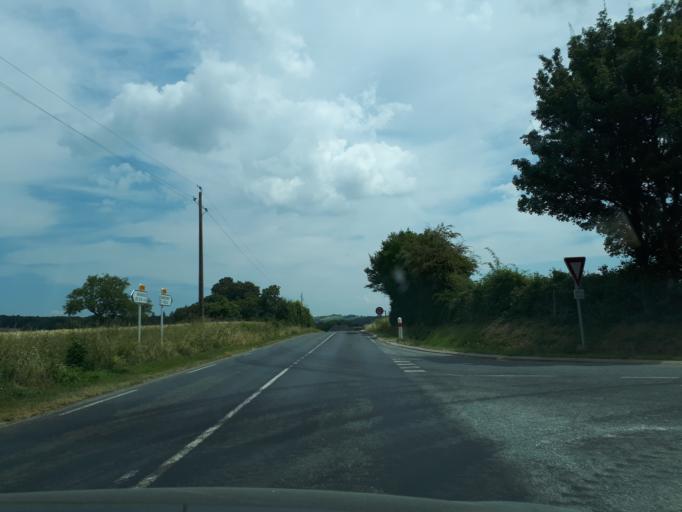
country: FR
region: Centre
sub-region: Departement du Cher
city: Rians
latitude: 47.2182
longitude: 2.6243
